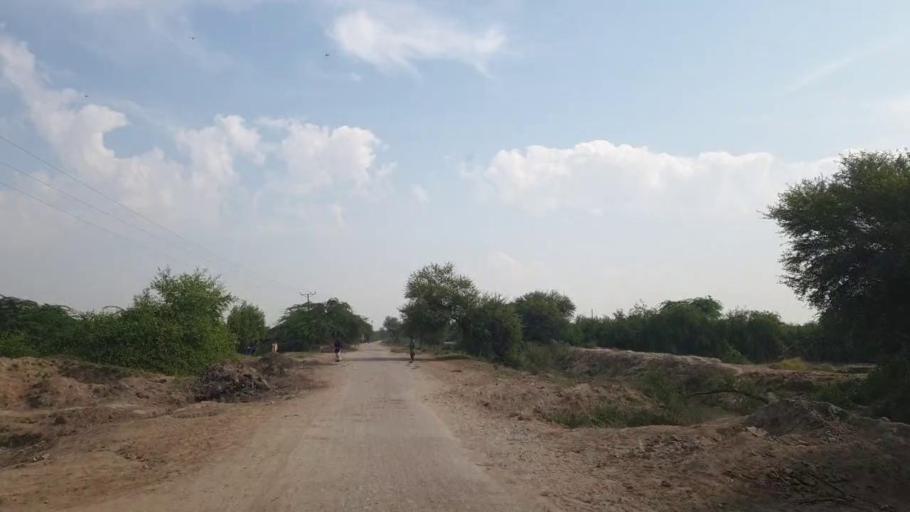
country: PK
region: Sindh
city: Tando Bago
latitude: 24.9243
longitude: 69.0193
